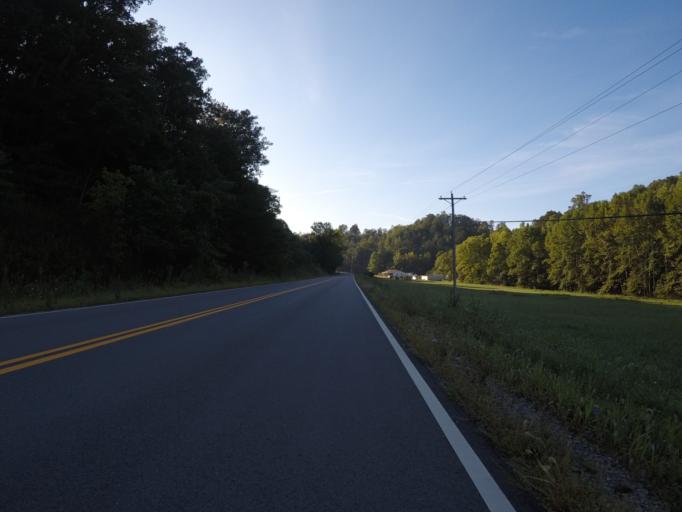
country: US
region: Ohio
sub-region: Lawrence County
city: Ironton
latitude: 38.6075
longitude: -82.5862
